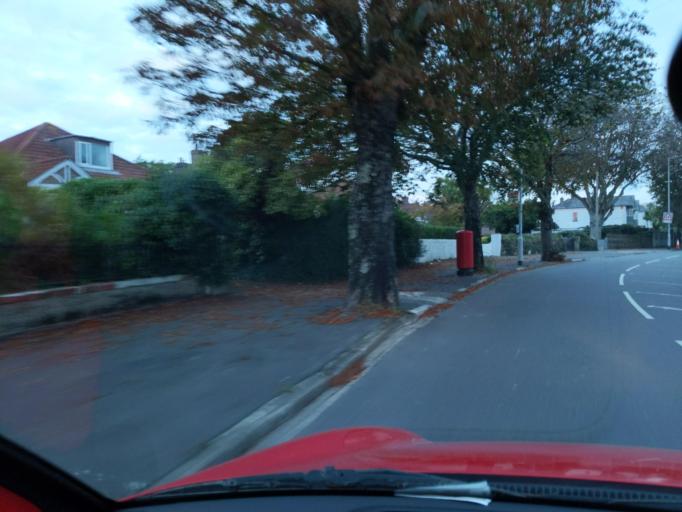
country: GB
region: England
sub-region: Plymouth
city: Plymouth
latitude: 50.3941
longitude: -4.1584
